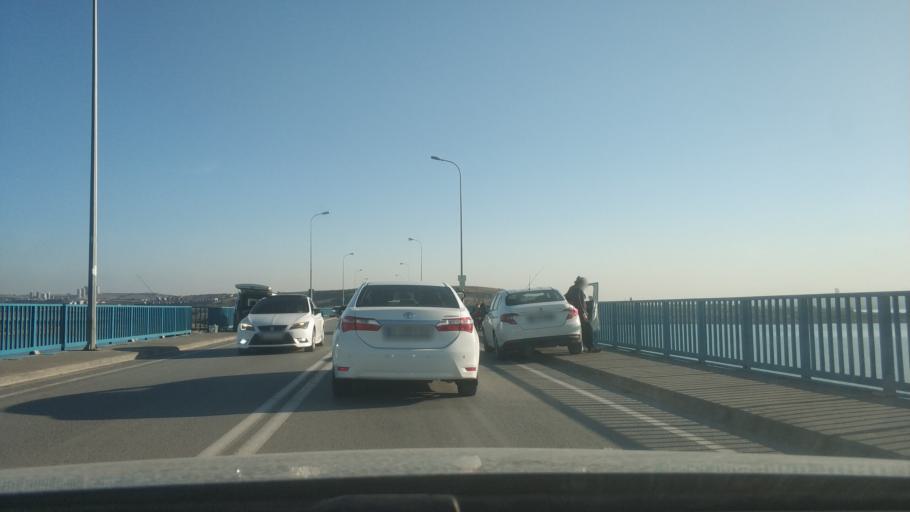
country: TR
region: Adana
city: Adana
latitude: 37.1023
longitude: 35.3011
